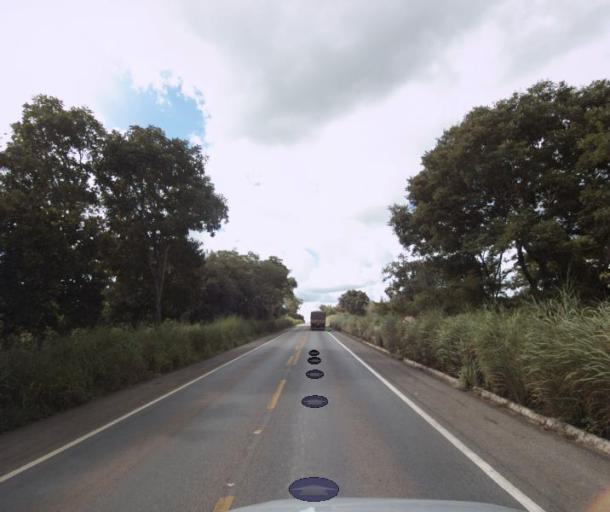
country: BR
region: Goias
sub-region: Porangatu
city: Porangatu
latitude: -13.3231
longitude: -49.1189
